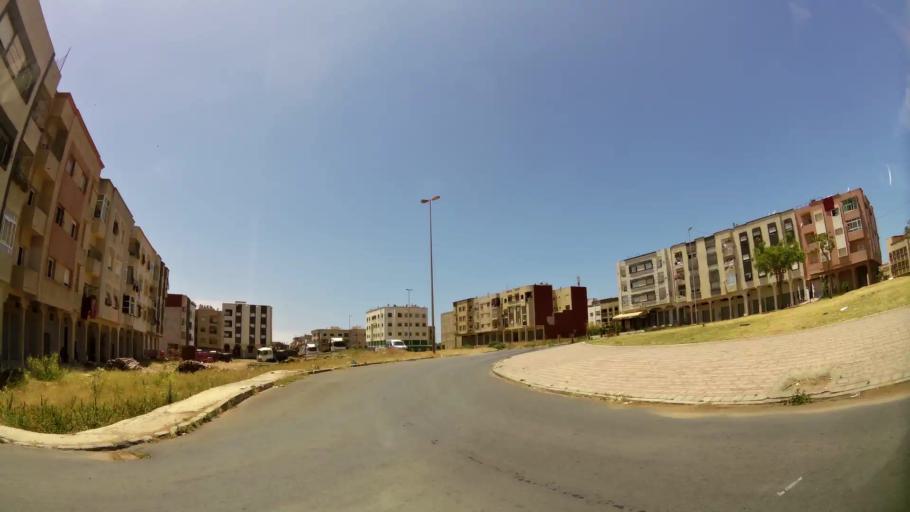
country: MA
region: Gharb-Chrarda-Beni Hssen
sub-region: Kenitra Province
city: Kenitra
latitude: 34.2536
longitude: -6.6199
